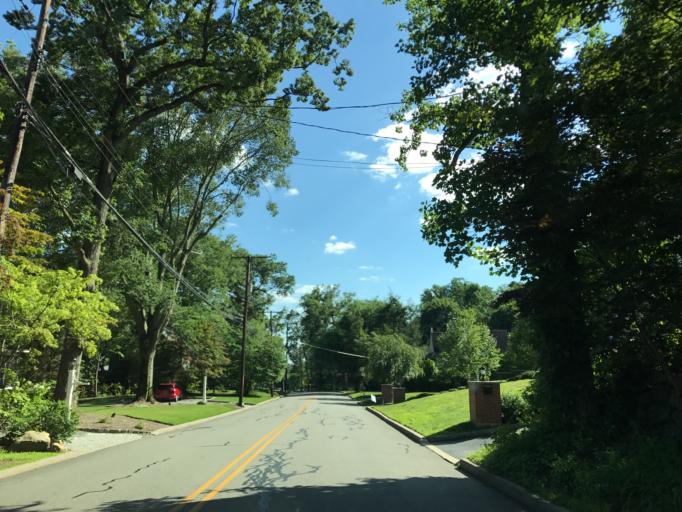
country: US
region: New Jersey
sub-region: Morris County
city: Boonton
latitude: 40.8999
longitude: -74.4170
